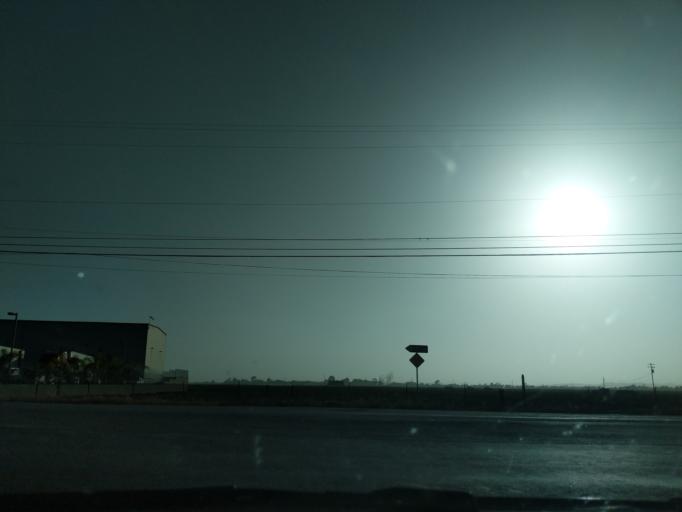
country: US
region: California
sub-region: Monterey County
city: Pajaro
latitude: 36.8911
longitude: -121.7473
